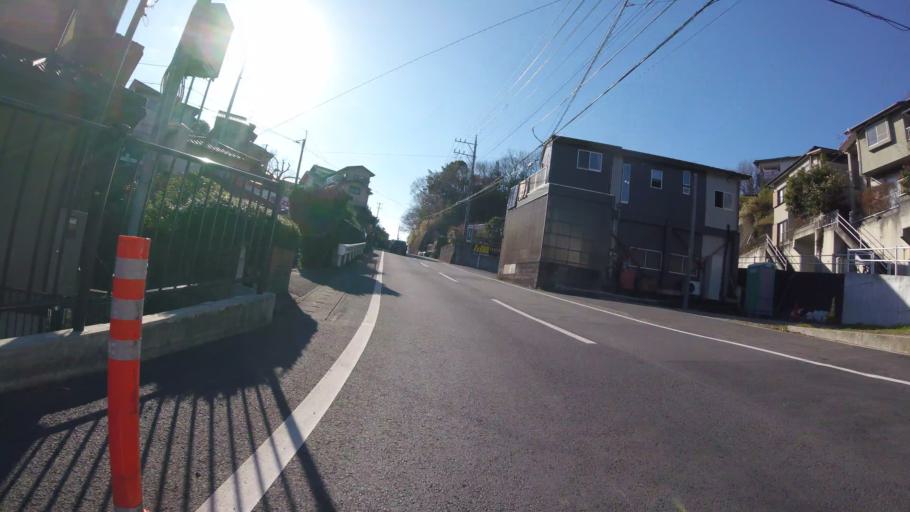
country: JP
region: Shizuoka
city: Mishima
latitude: 35.0883
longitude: 138.9638
